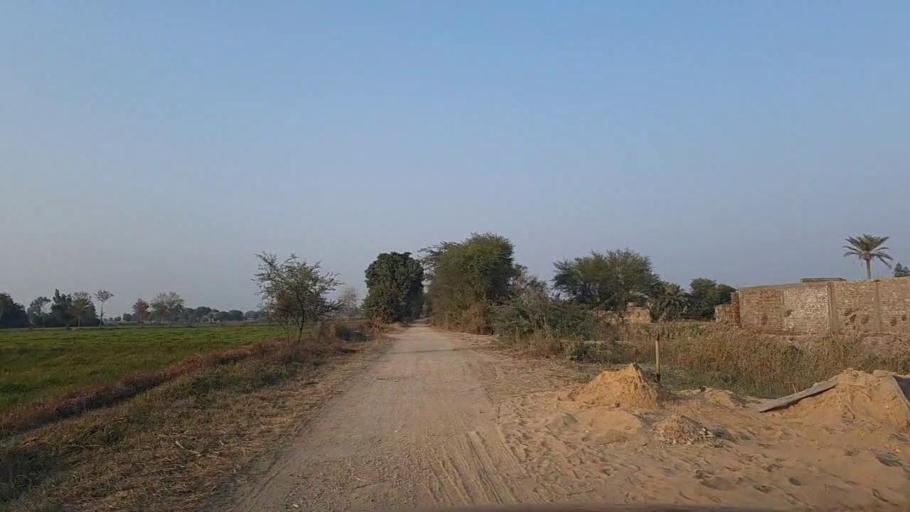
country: PK
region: Sindh
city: Daur
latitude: 26.4342
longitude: 68.3937
